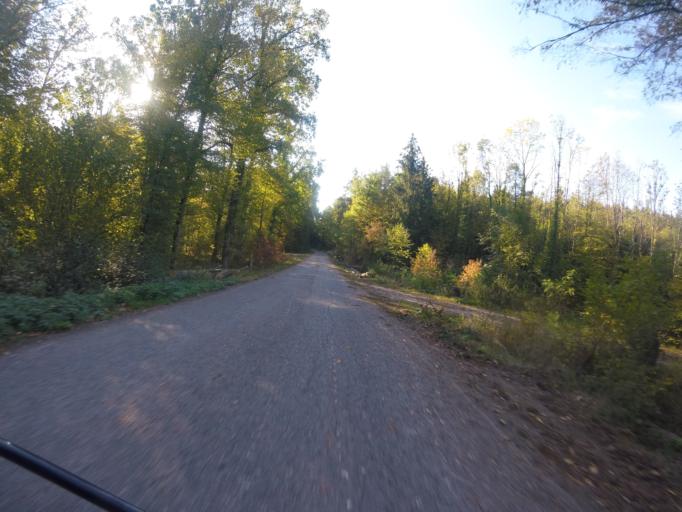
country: DE
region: Baden-Wuerttemberg
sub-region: Regierungsbezirk Stuttgart
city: Oppenweiler
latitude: 48.9940
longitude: 9.4275
